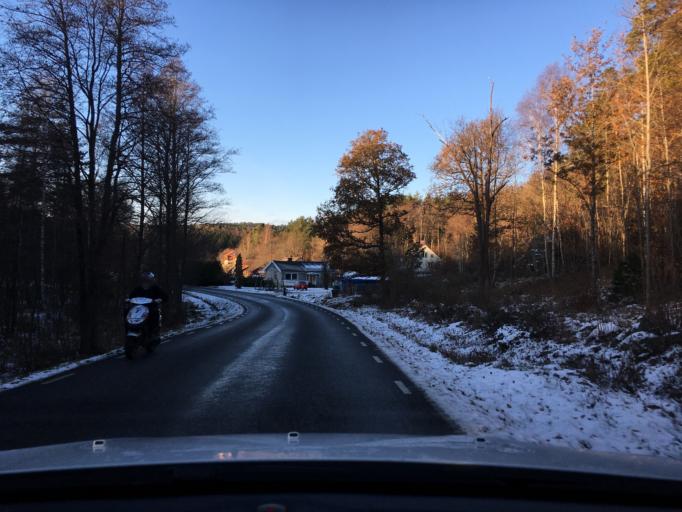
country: SE
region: Vaestra Goetaland
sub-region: Tjorns Kommun
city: Myggenas
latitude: 58.0579
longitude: 11.6927
